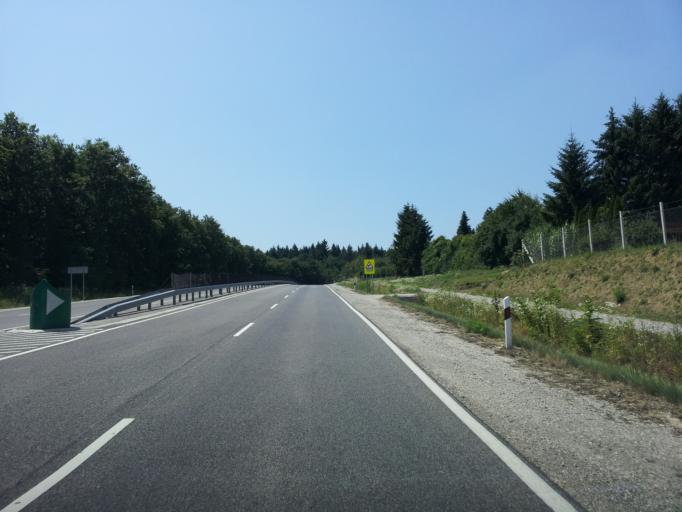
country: HU
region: Zala
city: Zalaegerszeg
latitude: 46.8426
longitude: 16.9026
